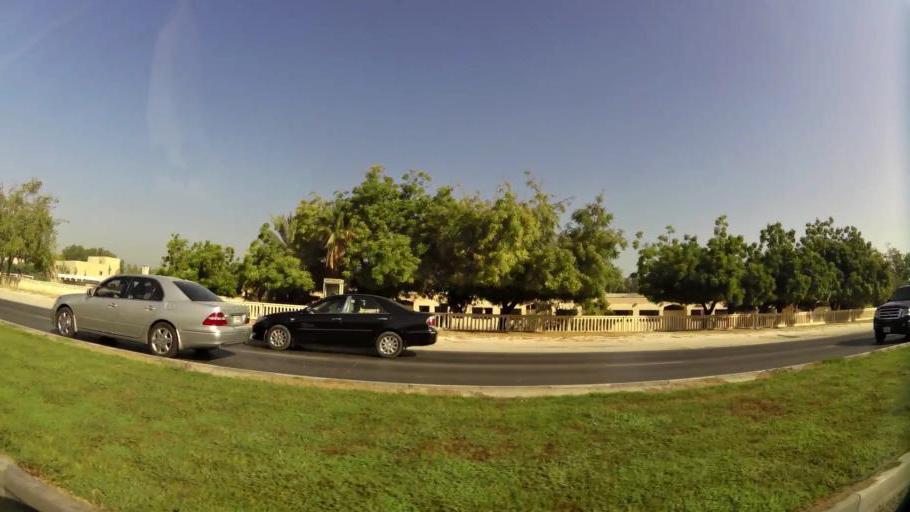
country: AE
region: Ajman
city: Ajman
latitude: 25.3802
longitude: 55.4051
